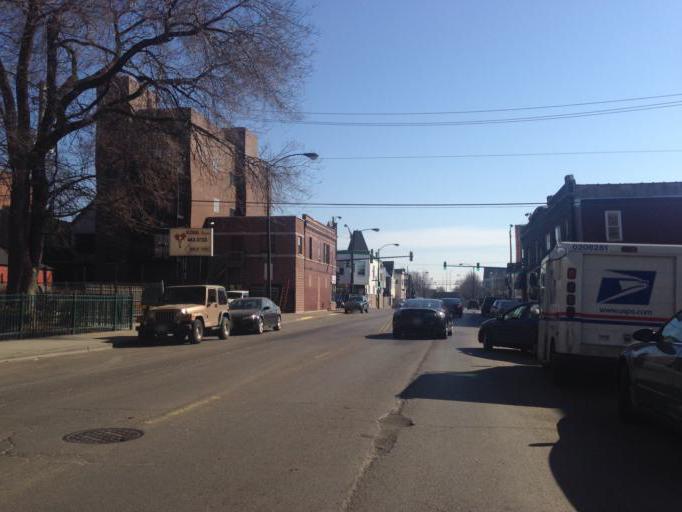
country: US
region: Illinois
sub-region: Cook County
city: Lincolnwood
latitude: 41.9401
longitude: -87.7027
